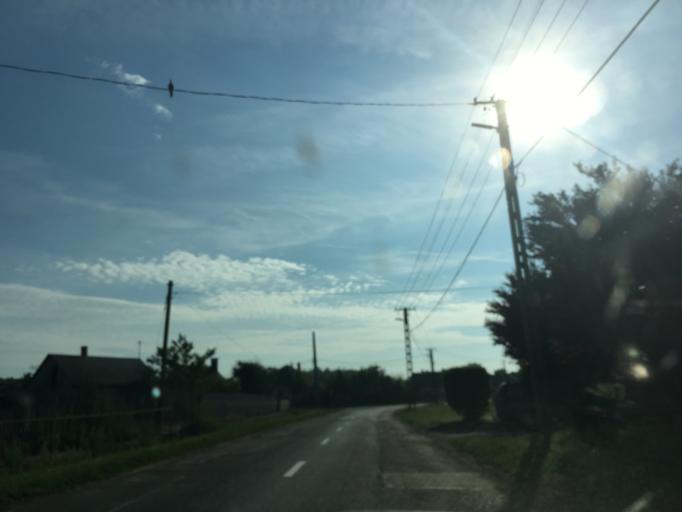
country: HU
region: Hajdu-Bihar
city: Nyiradony
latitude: 47.6908
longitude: 21.9194
